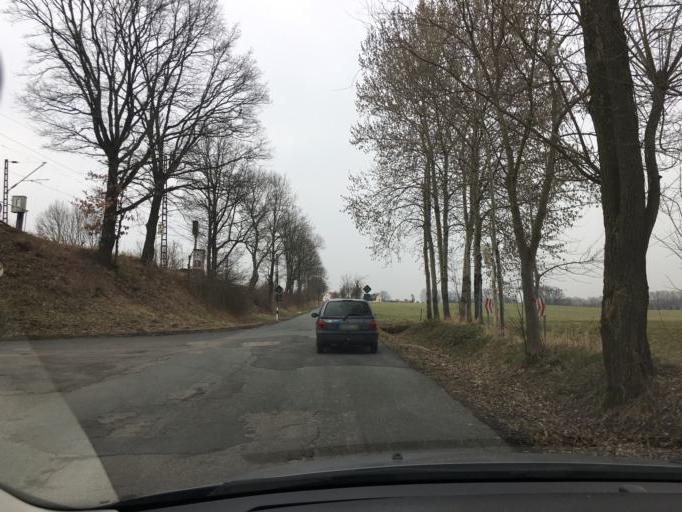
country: DE
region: Thuringia
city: Gerstenberg
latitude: 51.0415
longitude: 12.4400
